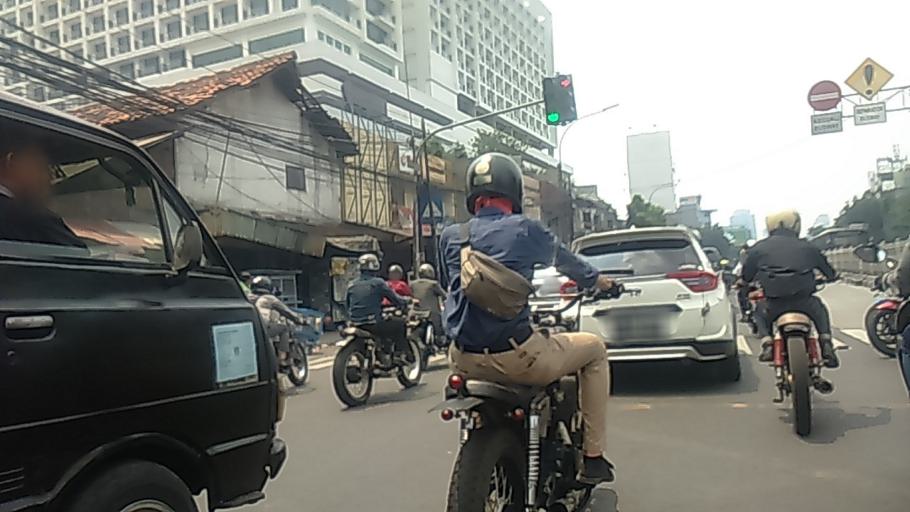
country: ID
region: Jakarta Raya
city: Jakarta
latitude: -6.2550
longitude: 106.8274
